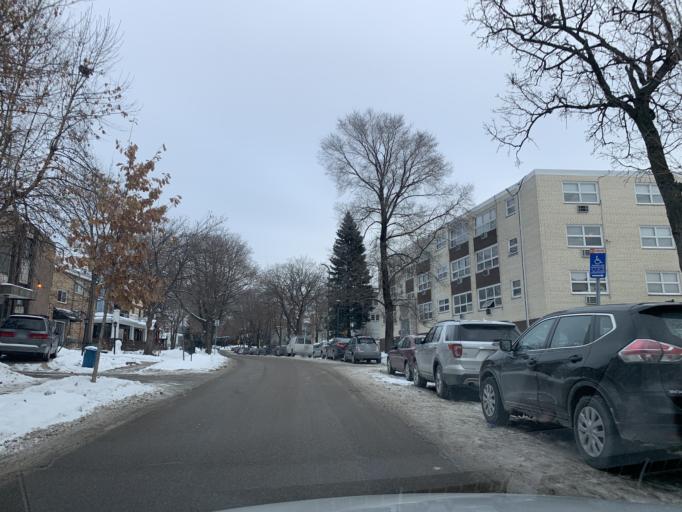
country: US
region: Minnesota
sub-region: Hennepin County
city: Minneapolis
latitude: 44.9635
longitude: -93.2860
